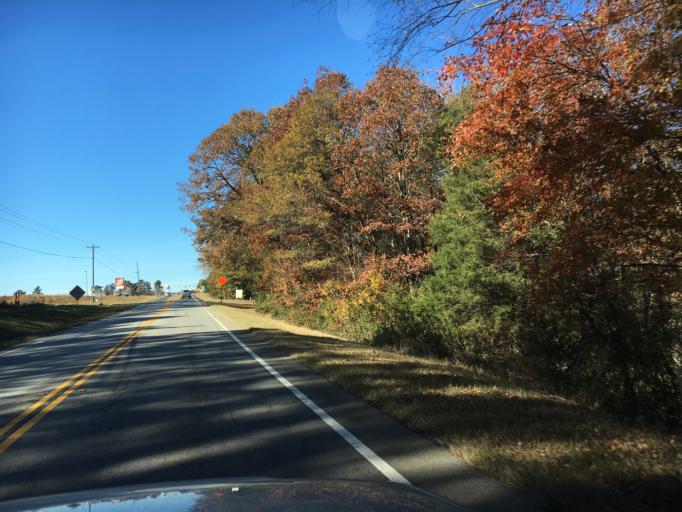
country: US
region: Georgia
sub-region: Hart County
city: Hartwell
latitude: 34.3487
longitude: -82.8989
